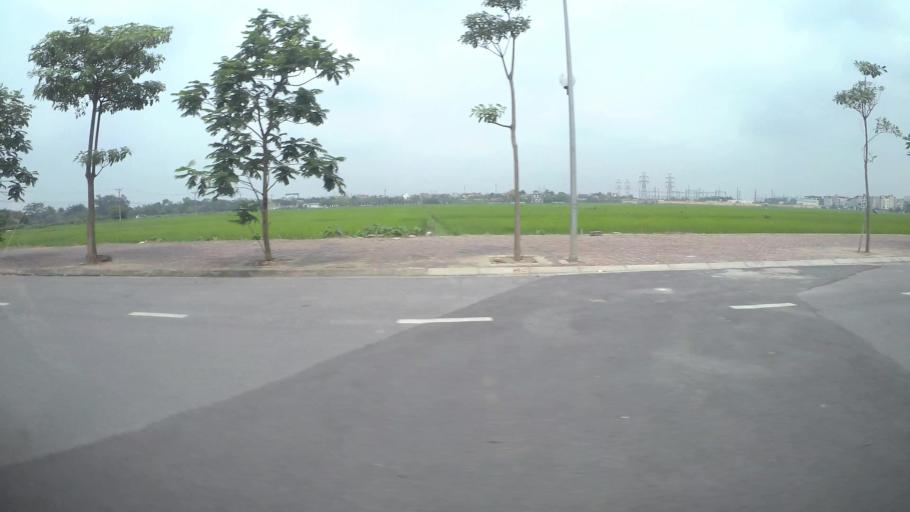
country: VN
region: Ha Noi
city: Trau Quy
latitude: 21.0692
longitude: 105.9109
